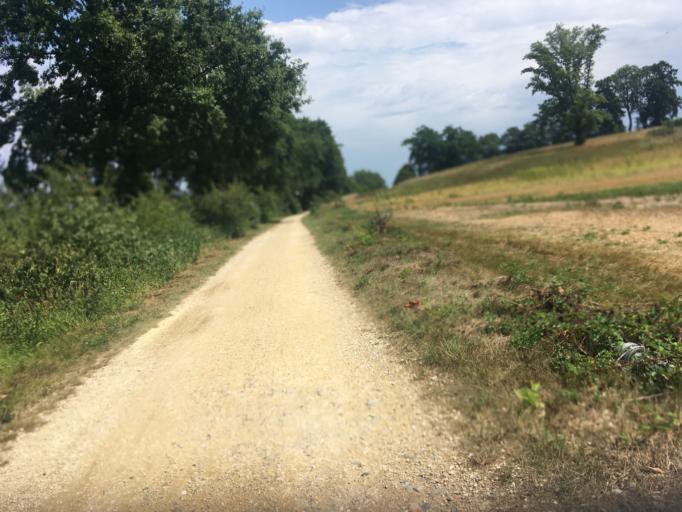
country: CH
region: Bern
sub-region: Biel/Bienne District
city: Orpund
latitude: 47.1340
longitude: 7.3085
